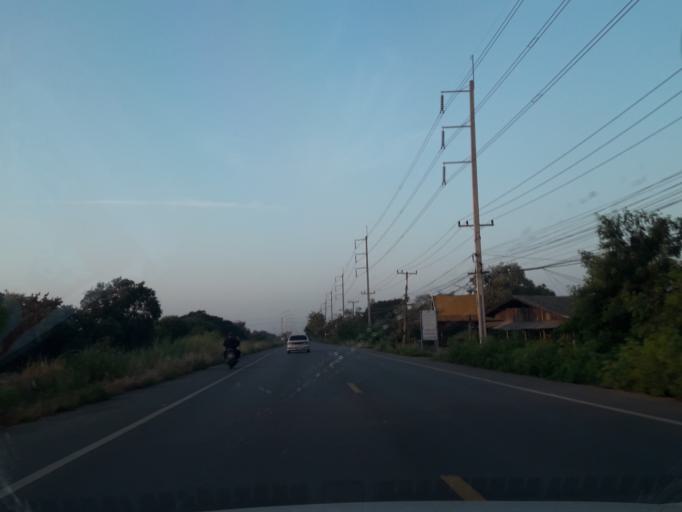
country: TH
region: Phra Nakhon Si Ayutthaya
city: Bang Pahan
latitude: 14.4782
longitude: 100.5545
